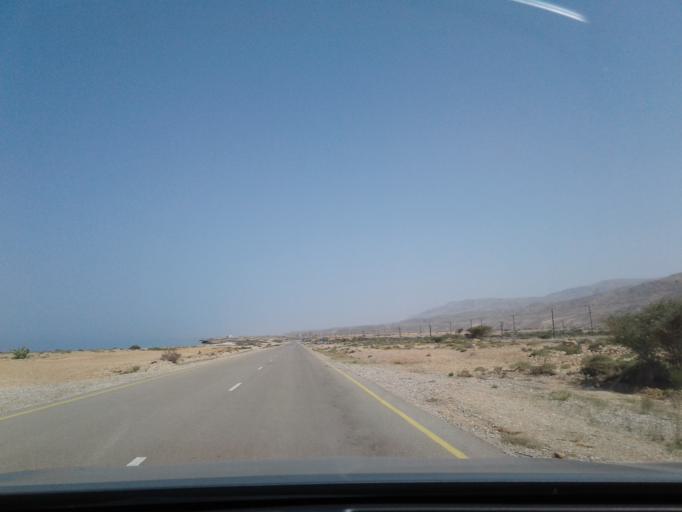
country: OM
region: Ash Sharqiyah
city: Al Qabil
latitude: 23.0380
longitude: 59.0764
